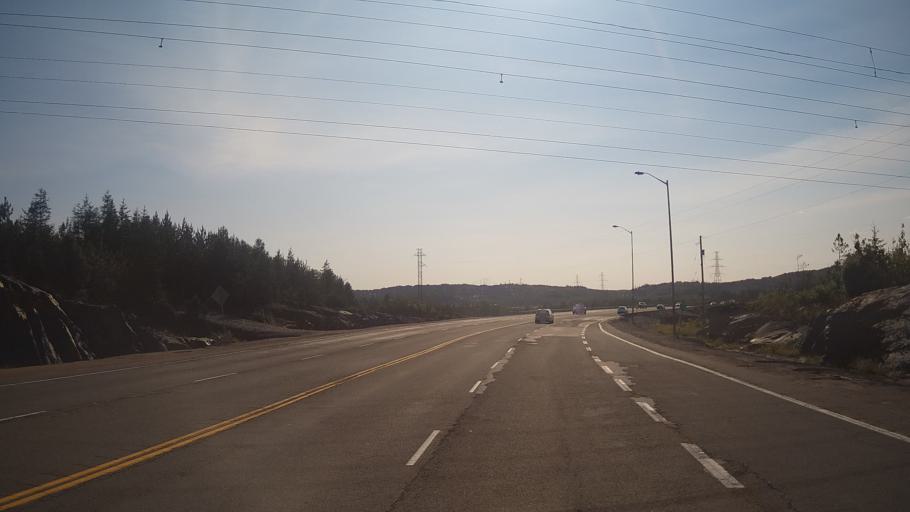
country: CA
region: Ontario
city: Greater Sudbury
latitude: 46.5029
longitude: -81.0385
